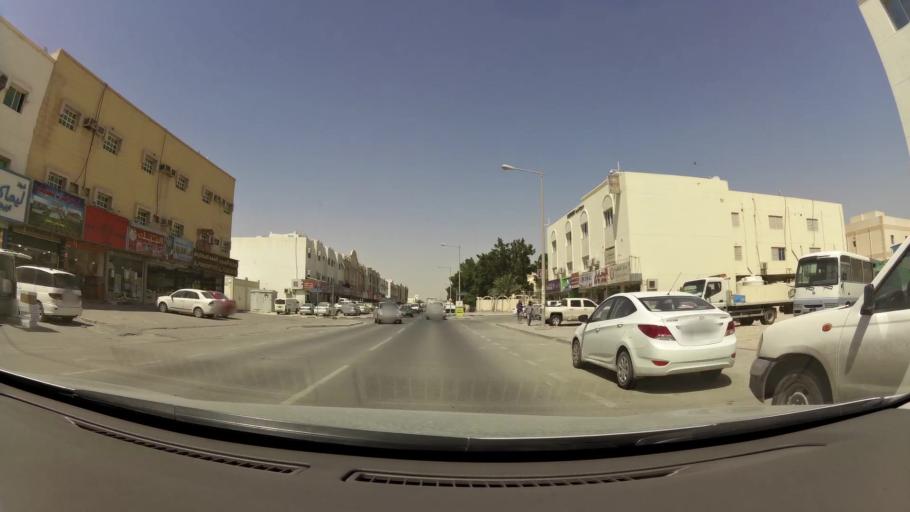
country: QA
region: Baladiyat ar Rayyan
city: Ar Rayyan
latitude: 25.2767
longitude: 51.4078
